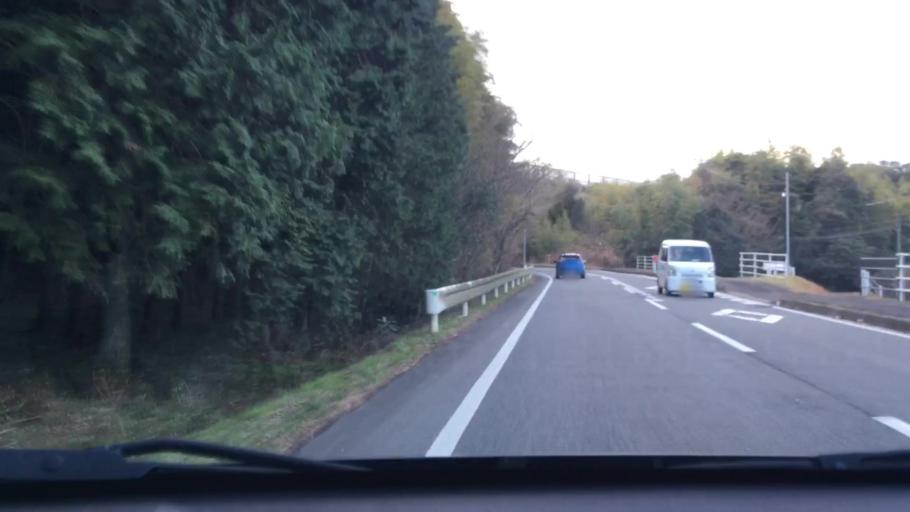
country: JP
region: Oita
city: Hiji
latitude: 33.3733
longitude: 131.4582
